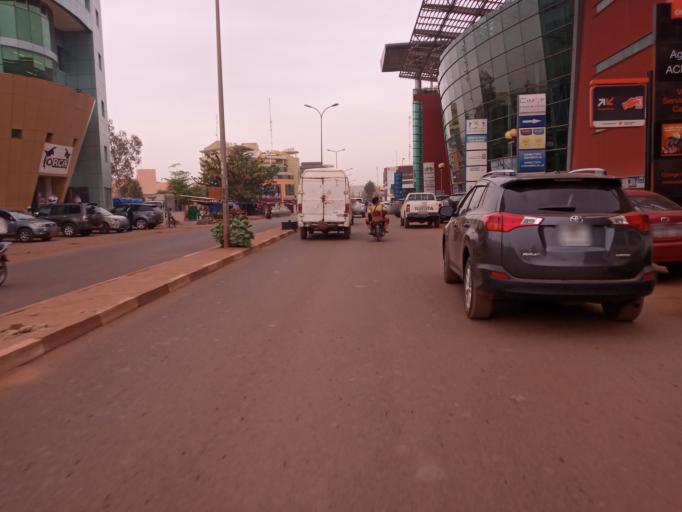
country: ML
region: Bamako
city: Bamako
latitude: 12.6326
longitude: -8.0278
